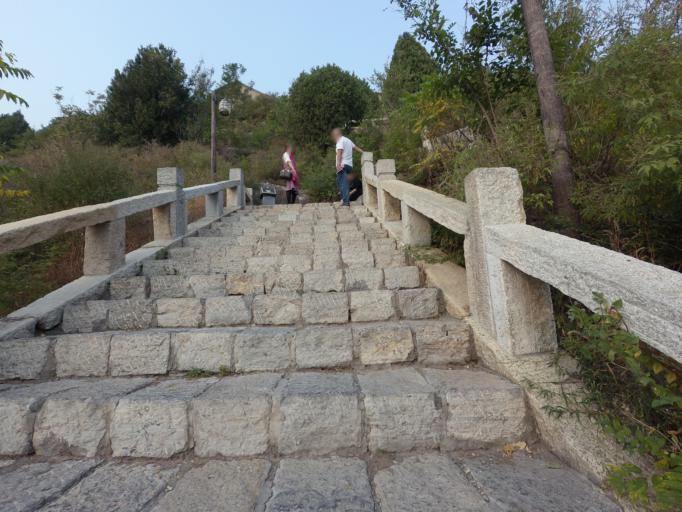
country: CN
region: Beijing
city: Xinchengzi
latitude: 40.6491
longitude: 117.2686
